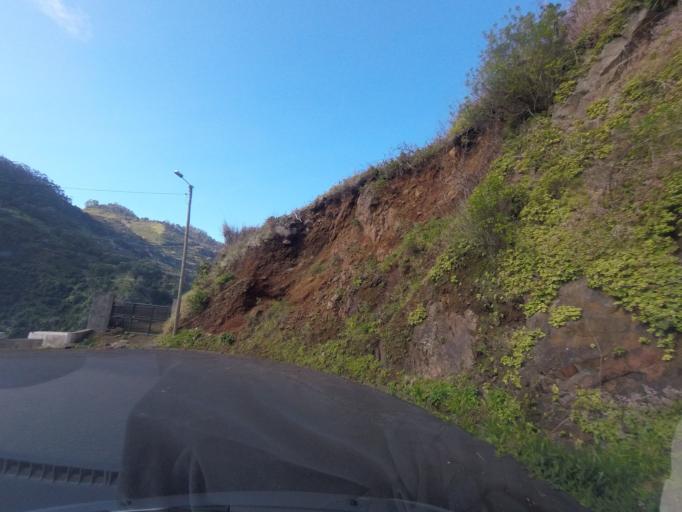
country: PT
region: Madeira
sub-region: Porto Moniz
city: Porto Moniz
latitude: 32.8491
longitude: -17.1571
